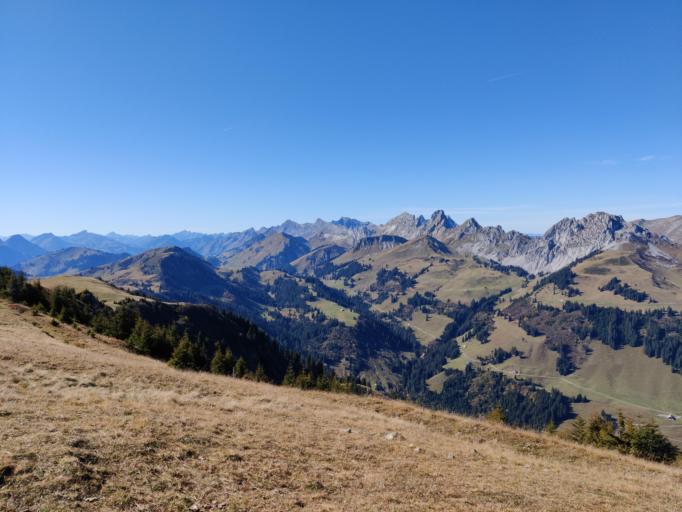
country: CH
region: Bern
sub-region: Obersimmental-Saanen District
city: Zweisimmen
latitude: 46.5569
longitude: 7.3050
